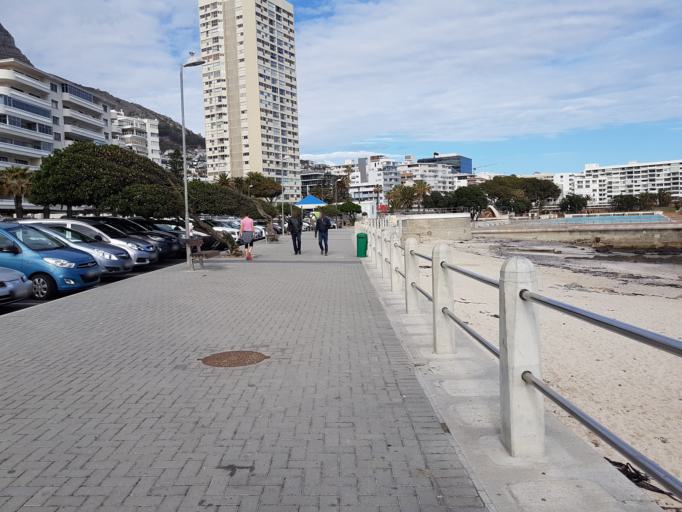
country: ZA
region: Western Cape
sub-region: City of Cape Town
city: Cape Town
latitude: -33.9173
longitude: 18.3861
